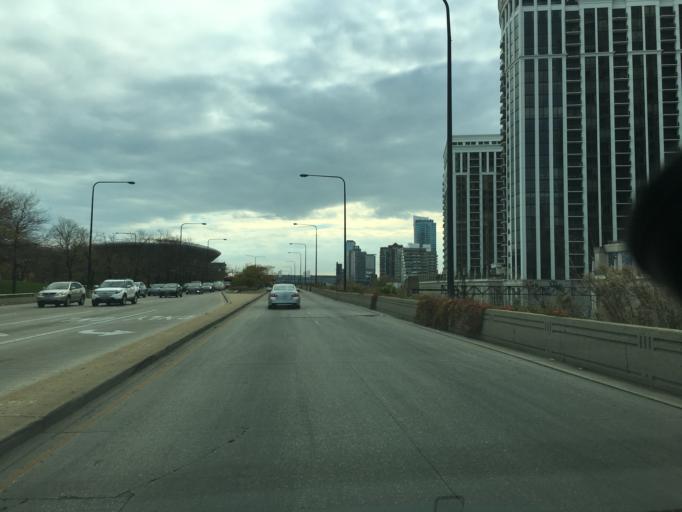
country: US
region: Illinois
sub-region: Cook County
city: Chicago
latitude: 41.8671
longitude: -87.6205
